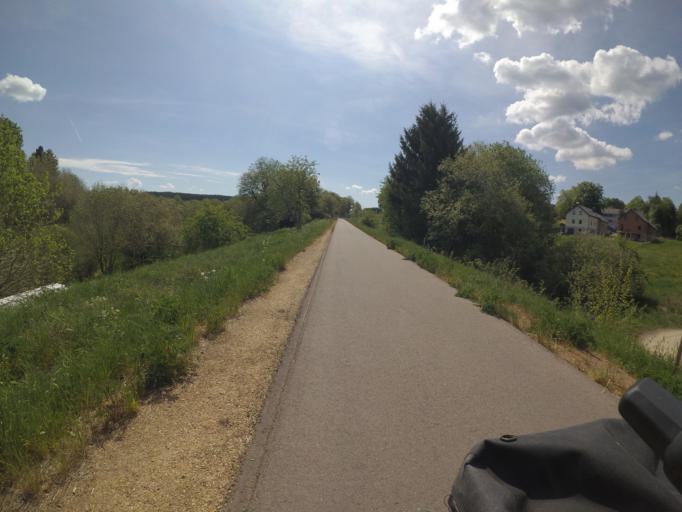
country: BE
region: Wallonia
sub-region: Province de Liege
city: Bullange
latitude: 50.4083
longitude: 6.2641
